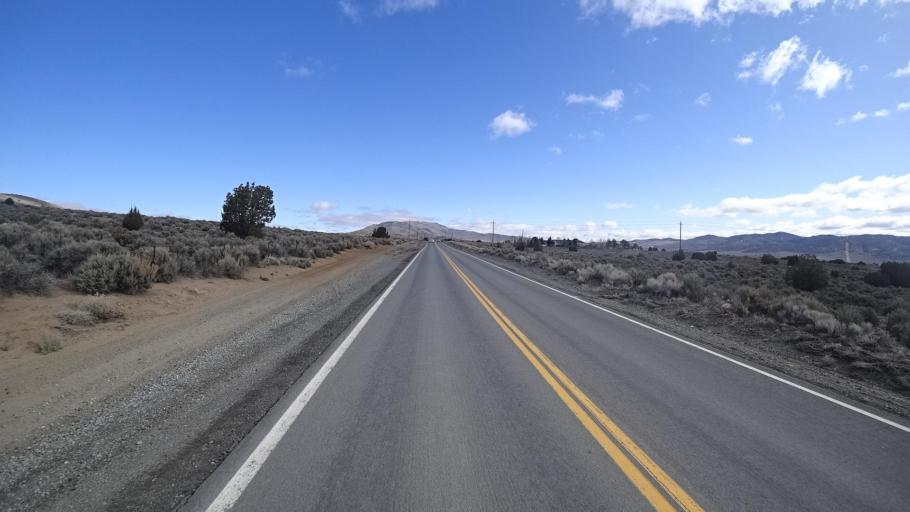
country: US
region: Nevada
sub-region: Washoe County
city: Cold Springs
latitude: 39.7088
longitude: -119.9048
